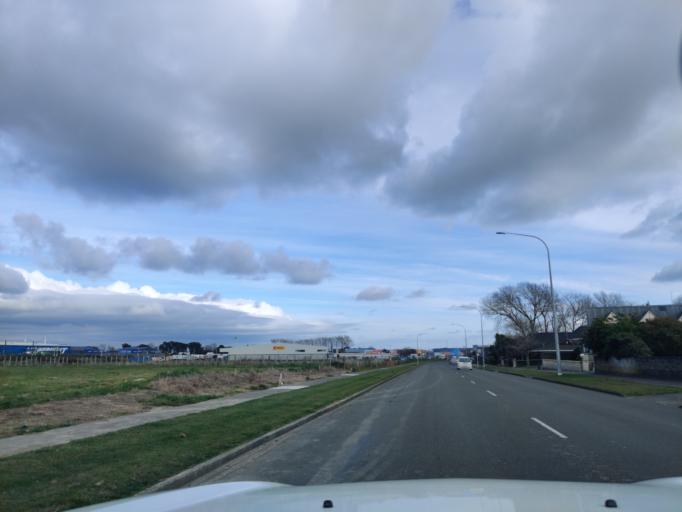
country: NZ
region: Manawatu-Wanganui
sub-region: Palmerston North City
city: Palmerston North
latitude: -40.3372
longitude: 175.6044
